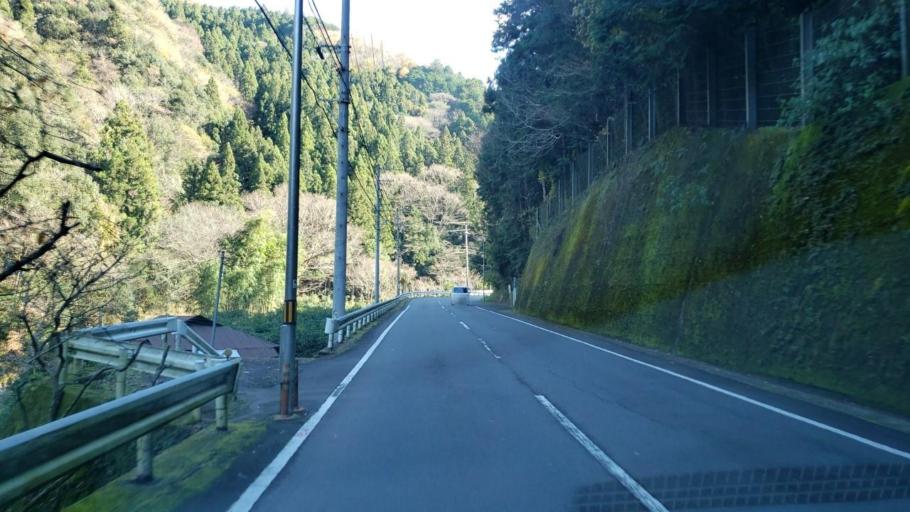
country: JP
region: Tokushima
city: Wakimachi
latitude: 34.0101
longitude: 134.0312
